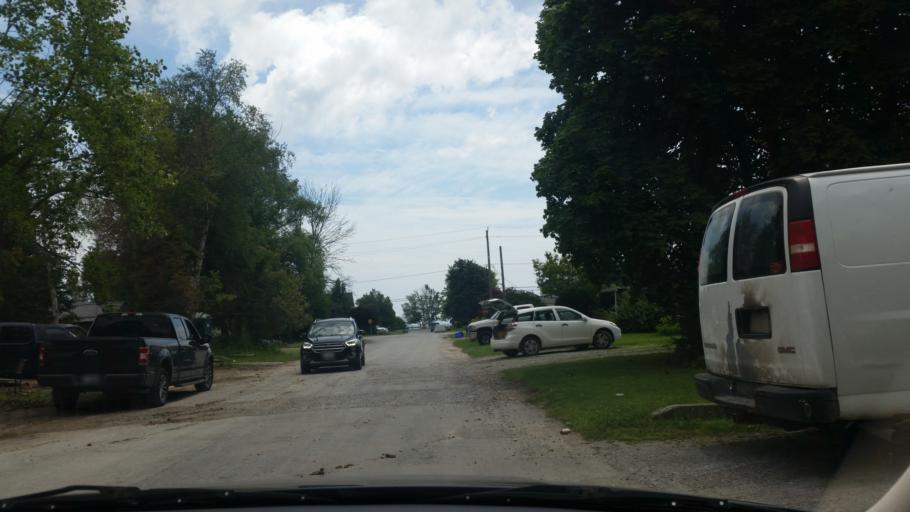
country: CA
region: Ontario
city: Norfolk County
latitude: 42.7892
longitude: -80.1801
